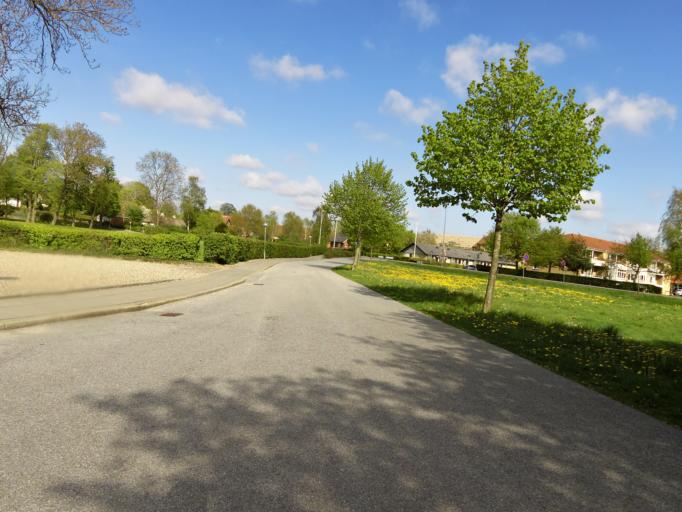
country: DK
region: South Denmark
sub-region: Vejen Kommune
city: Rodding
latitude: 55.3680
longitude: 9.0527
